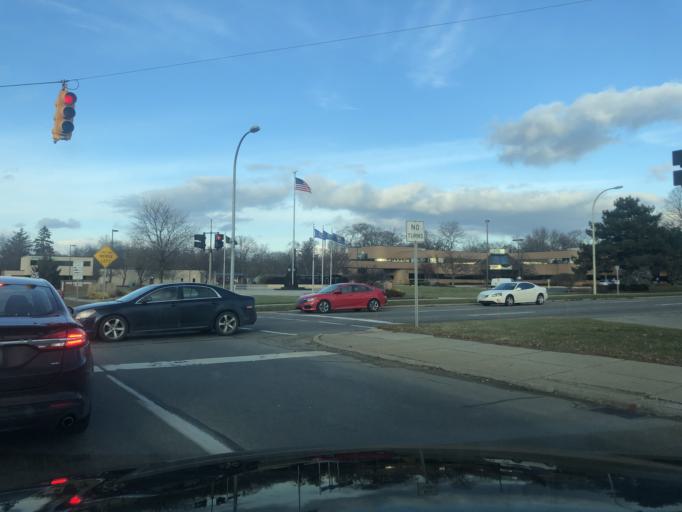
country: US
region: Michigan
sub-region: Wayne County
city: Livonia
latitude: 42.3971
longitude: -83.3734
